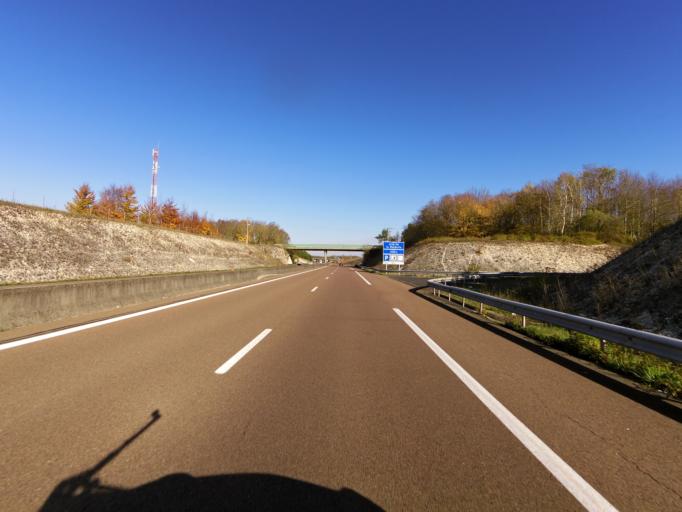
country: FR
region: Champagne-Ardenne
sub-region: Departement de la Marne
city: Compertrix
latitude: 48.8773
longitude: 4.2898
